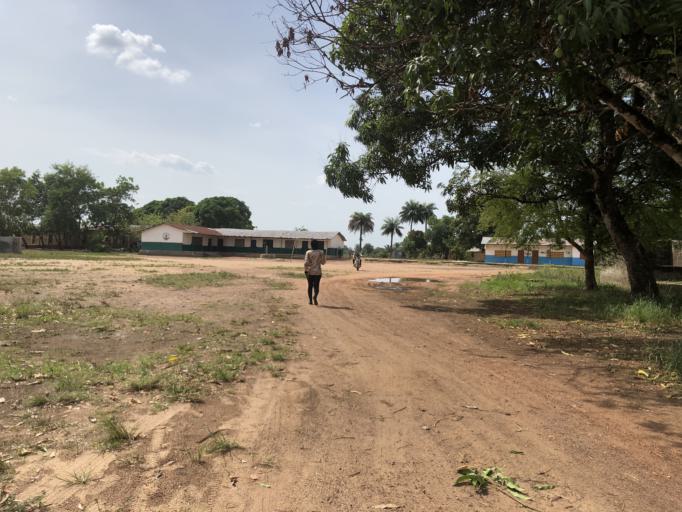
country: SL
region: Northern Province
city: Yonibana
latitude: 8.4655
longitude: -12.2223
